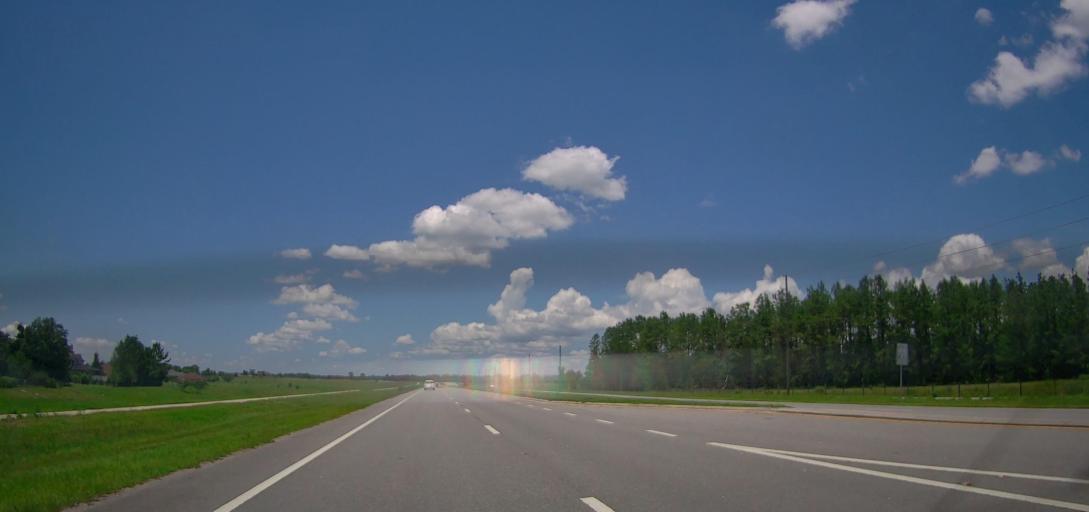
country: US
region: Florida
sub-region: Marion County
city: Silver Springs Shores
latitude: 29.0793
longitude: -82.0361
